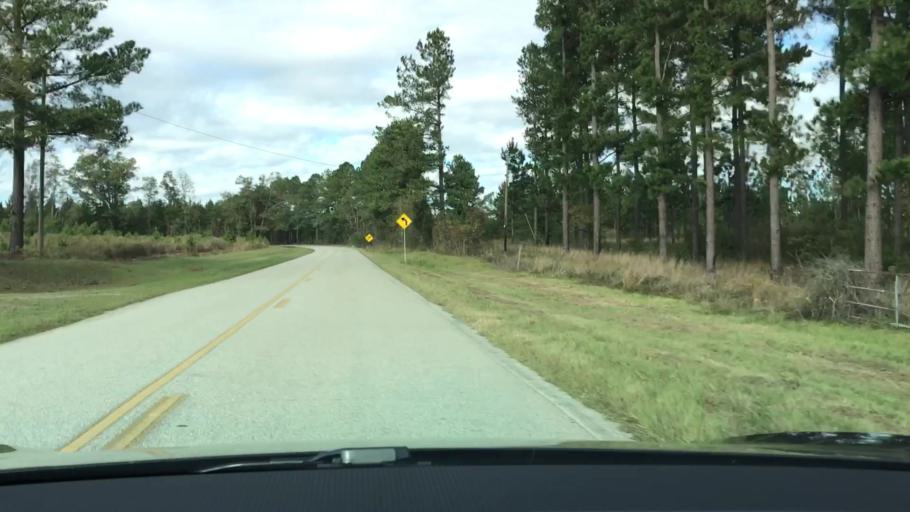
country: US
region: Georgia
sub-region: Jefferson County
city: Wadley
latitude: 32.8062
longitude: -82.3907
